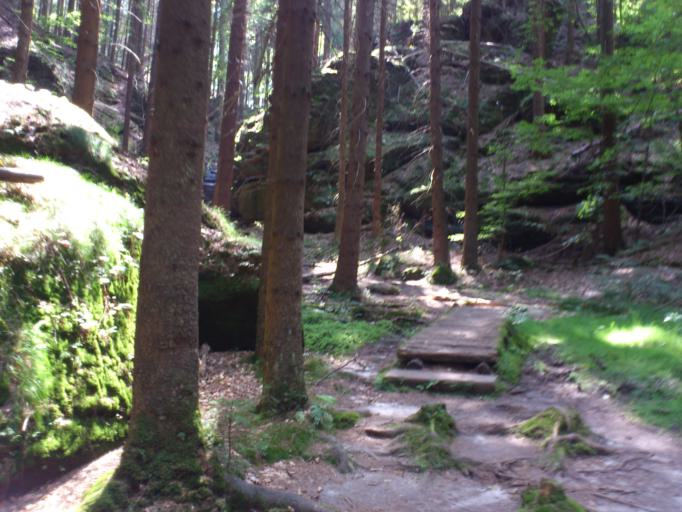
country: DE
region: Saxony
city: Sebnitz
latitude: 50.9199
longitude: 14.2843
